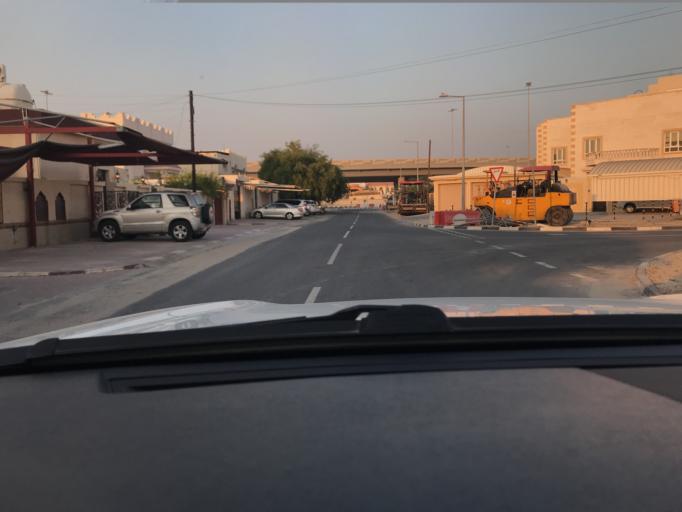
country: QA
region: Baladiyat ad Dawhah
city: Doha
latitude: 25.2532
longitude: 51.5059
